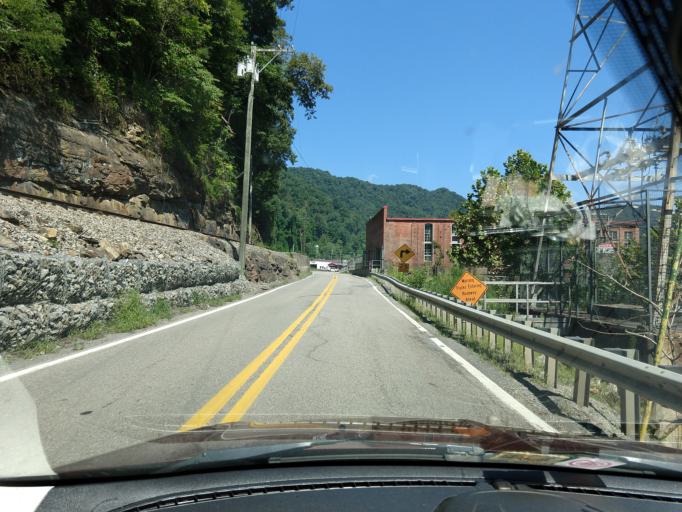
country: US
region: West Virginia
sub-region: Fayette County
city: Ansted
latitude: 38.1474
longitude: -81.2145
